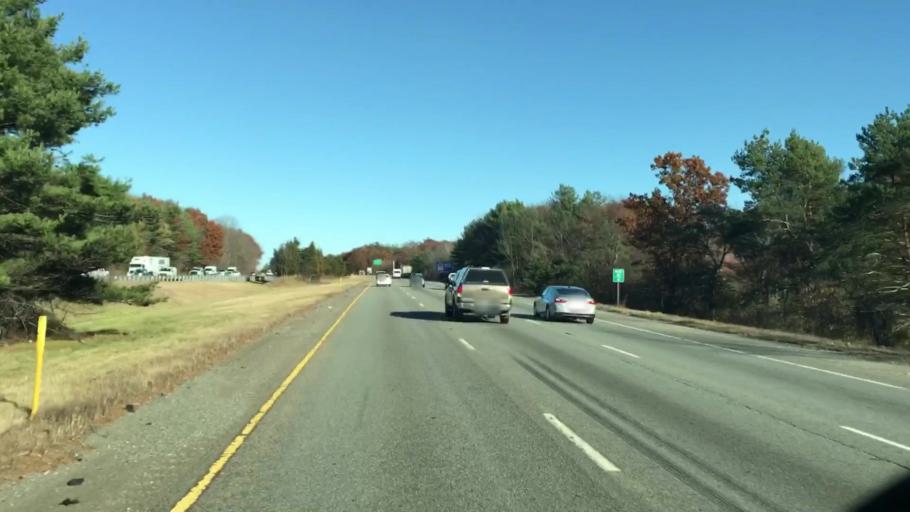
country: US
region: Massachusetts
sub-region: Middlesex County
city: Westford
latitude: 42.5560
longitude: -71.4487
